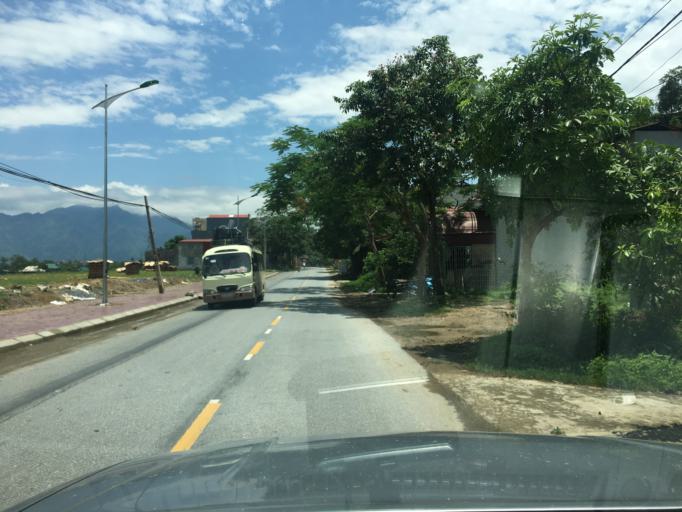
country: VN
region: Yen Bai
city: Son Thinh
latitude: 21.6183
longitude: 104.5084
